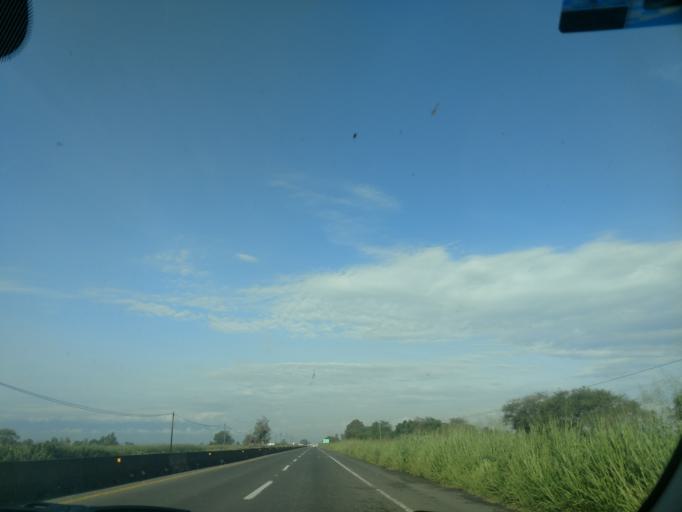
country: MX
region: Jalisco
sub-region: Ameca
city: Los Pocitos
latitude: 20.5358
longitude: -103.9504
